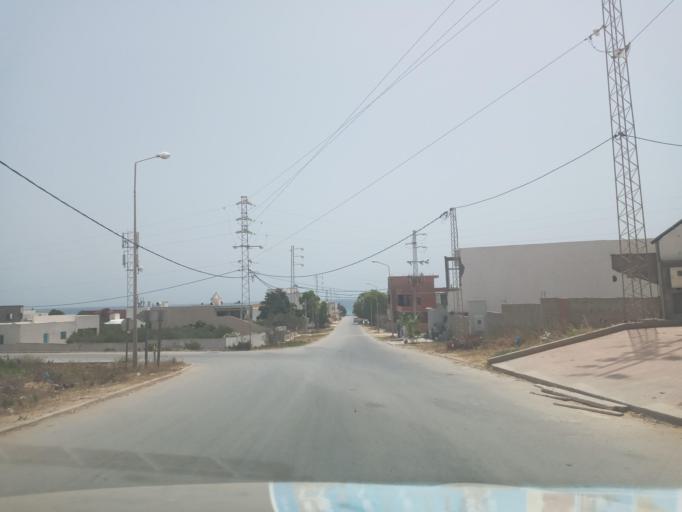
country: TN
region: Nabul
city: El Haouaria
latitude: 37.0370
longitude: 11.0510
